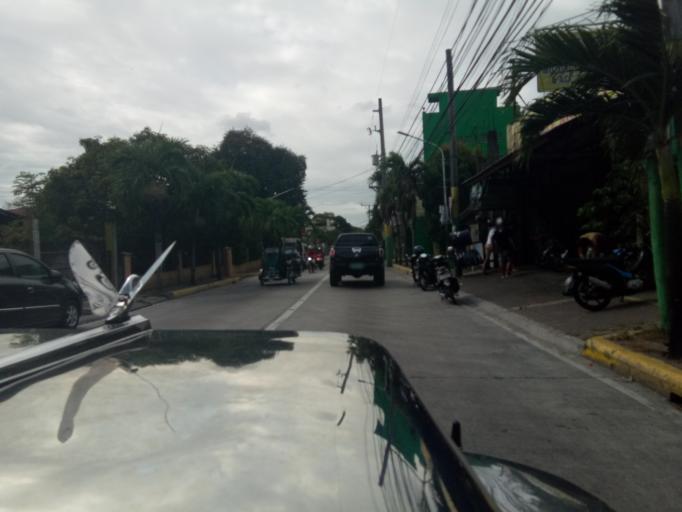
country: PH
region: Calabarzon
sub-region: Province of Cavite
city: Dasmarinas
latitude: 14.3216
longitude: 120.9391
